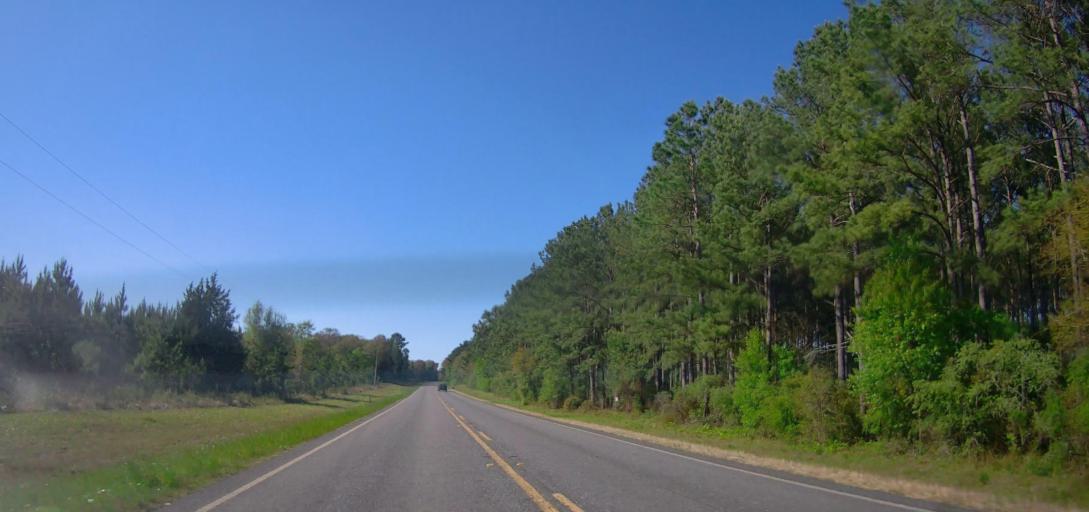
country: US
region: Georgia
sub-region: Wilcox County
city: Rochelle
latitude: 32.0256
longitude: -83.5008
